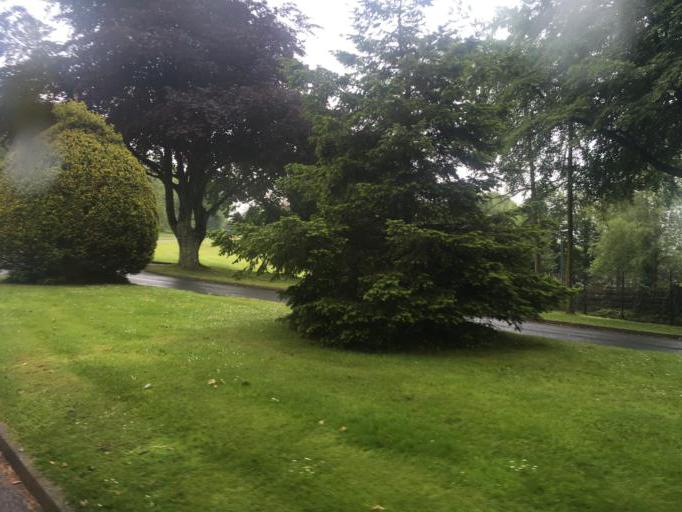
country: GB
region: England
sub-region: Devon
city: Dartmouth
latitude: 50.3552
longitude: -3.5815
